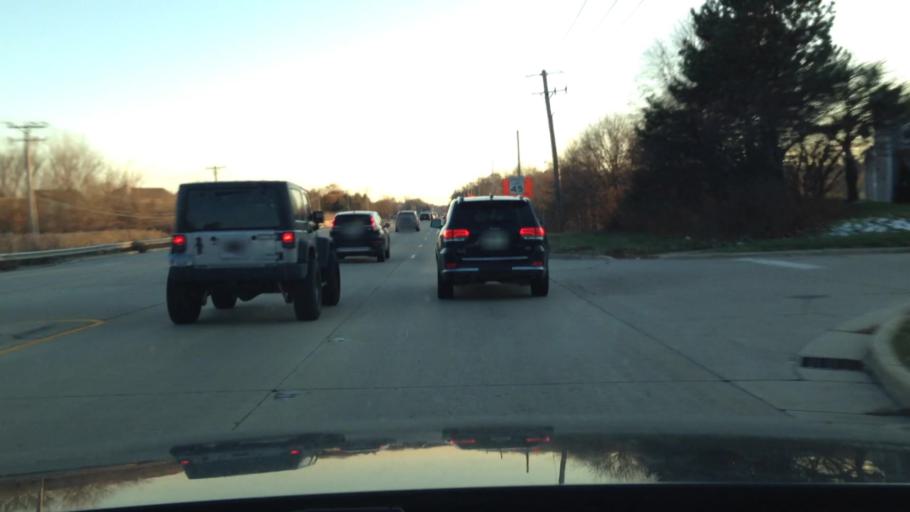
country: US
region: Illinois
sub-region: Cook County
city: Streamwood
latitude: 42.0254
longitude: -88.2031
